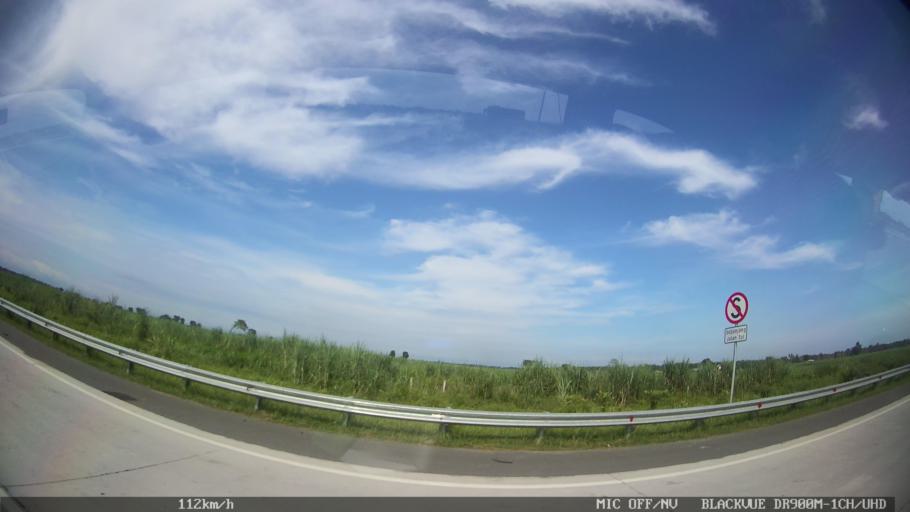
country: ID
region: North Sumatra
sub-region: Kabupaten Langkat
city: Stabat
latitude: 3.6957
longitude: 98.5404
